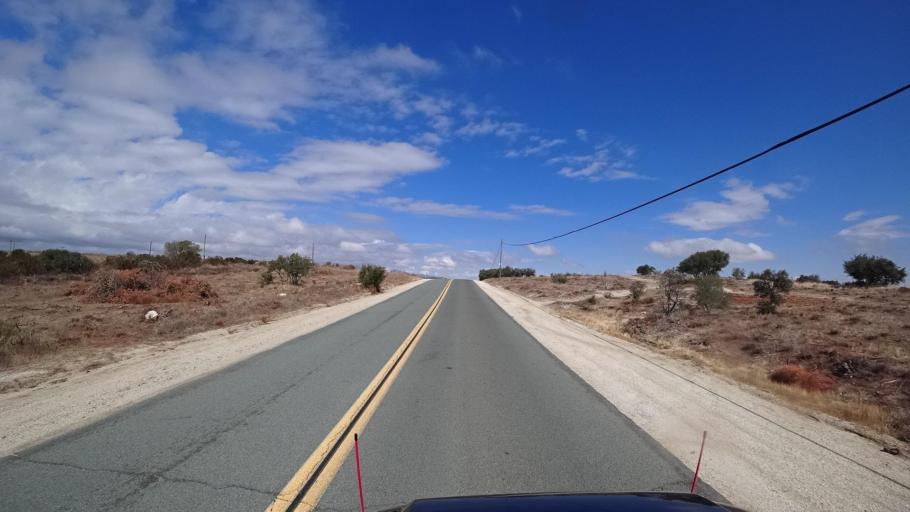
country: US
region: California
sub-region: San Diego County
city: Campo
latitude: 32.6566
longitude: -116.3150
